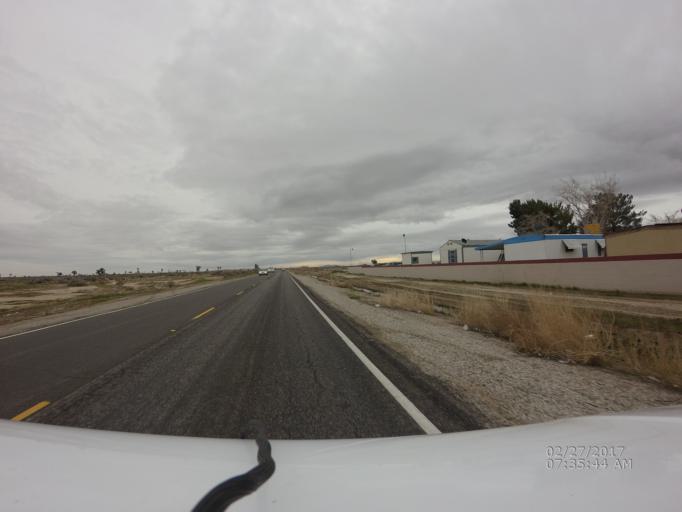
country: US
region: California
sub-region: Los Angeles County
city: Lancaster
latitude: 34.7188
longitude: -118.1086
